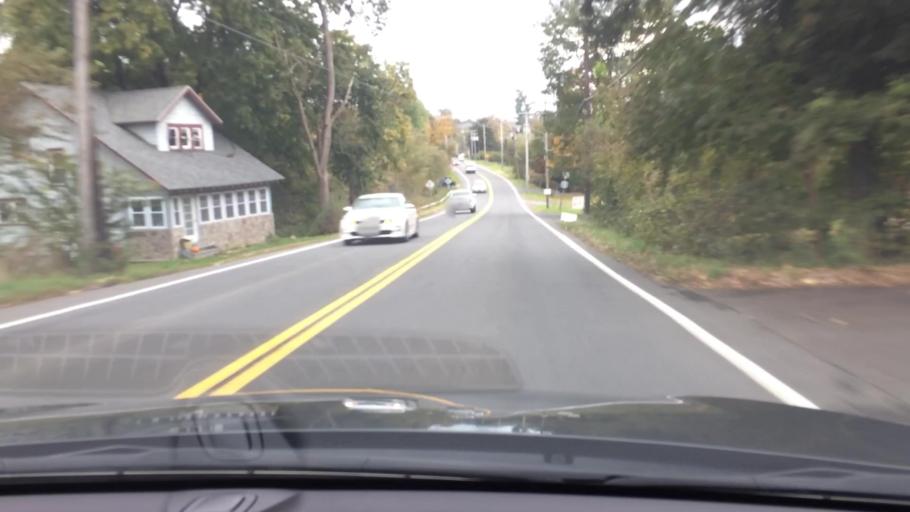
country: US
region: New York
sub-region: Columbia County
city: Lorenz Park
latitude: 42.2212
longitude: -73.7342
